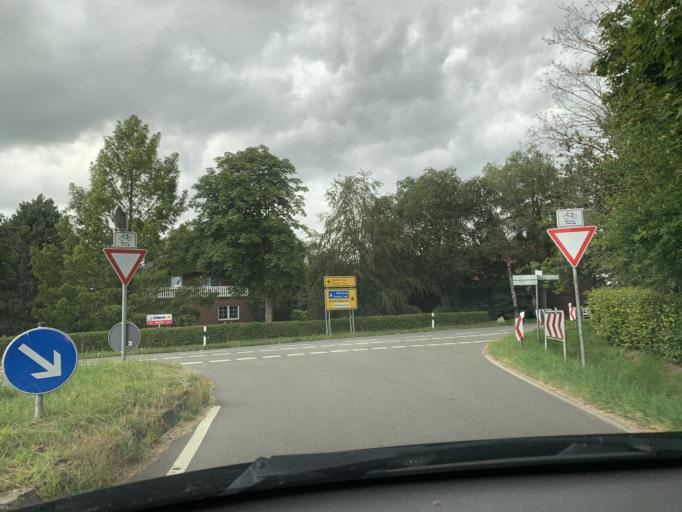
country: DE
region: Lower Saxony
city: Westerstede
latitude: 53.2256
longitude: 7.9013
